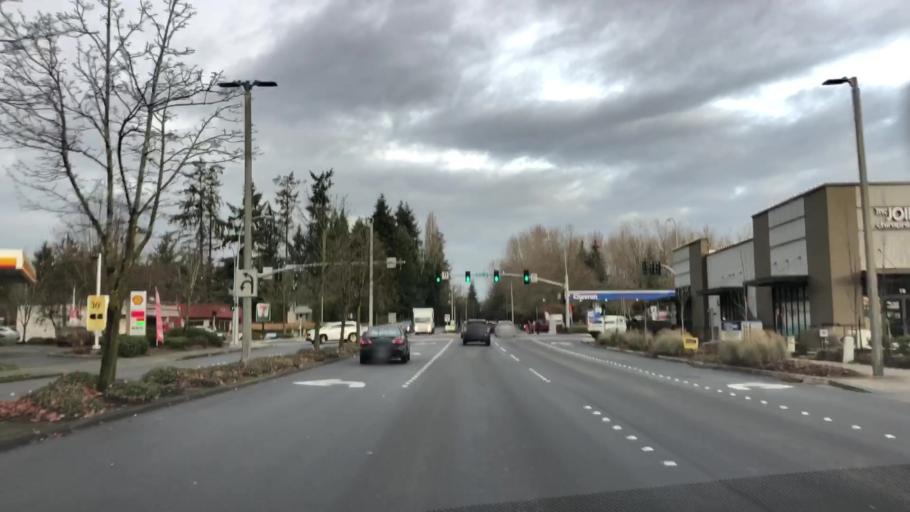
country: US
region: Washington
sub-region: King County
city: Eastgate
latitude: 47.6092
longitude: -122.1429
